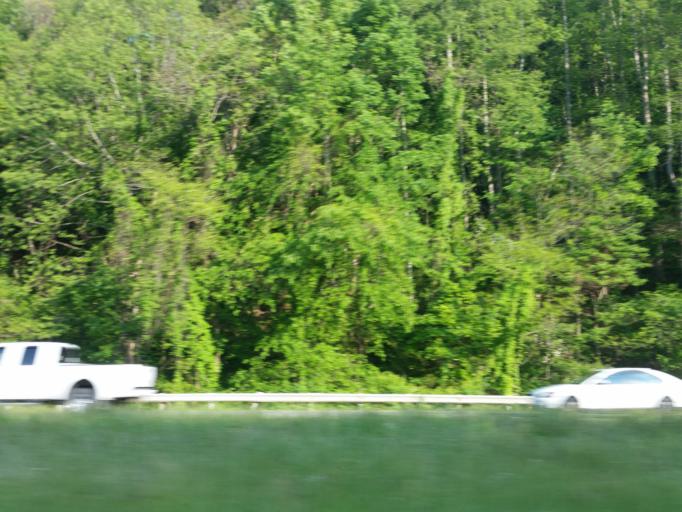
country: US
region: Virginia
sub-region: Russell County
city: Honaker
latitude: 36.9298
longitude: -81.9927
